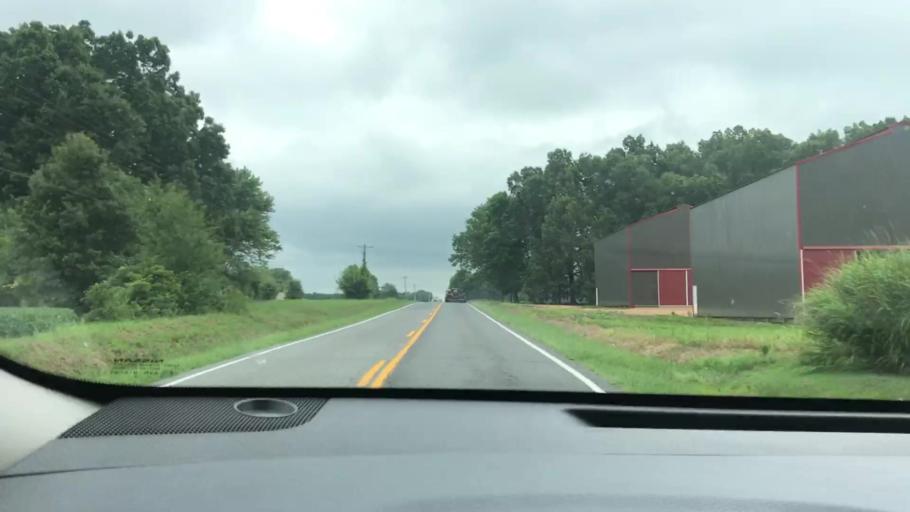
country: US
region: Kentucky
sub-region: Calloway County
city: Murray
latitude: 36.5769
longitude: -88.2324
